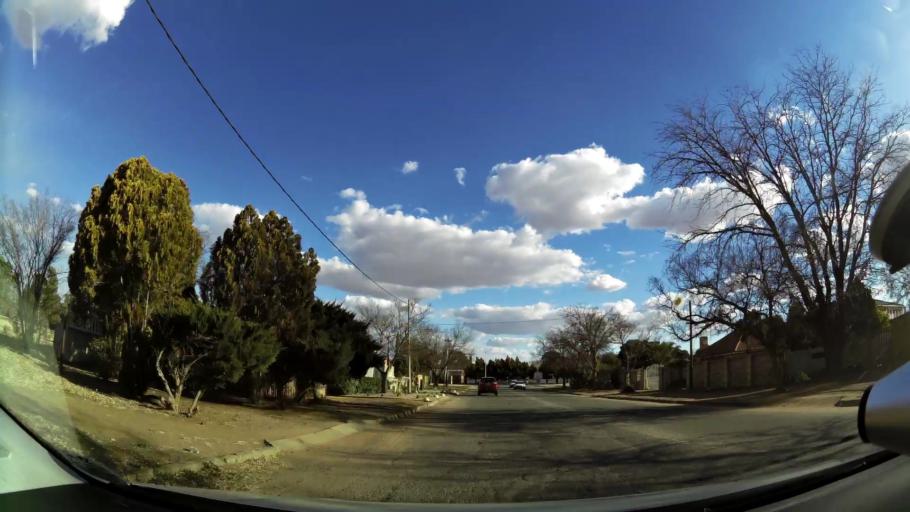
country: ZA
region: North-West
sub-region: Dr Kenneth Kaunda District Municipality
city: Klerksdorp
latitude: -26.8452
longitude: 26.6630
